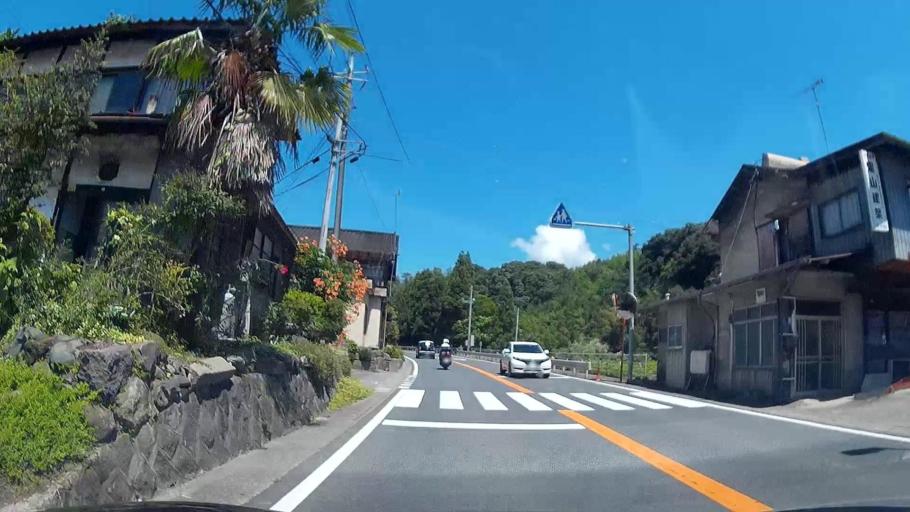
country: JP
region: Gunma
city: Numata
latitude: 36.6200
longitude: 139.0408
